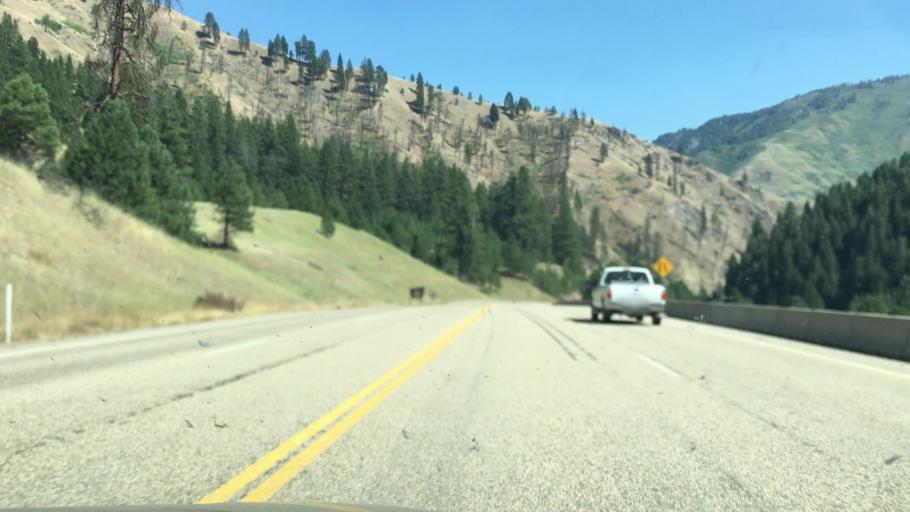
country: US
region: Idaho
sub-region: Boise County
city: Idaho City
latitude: 44.1119
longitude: -116.1022
